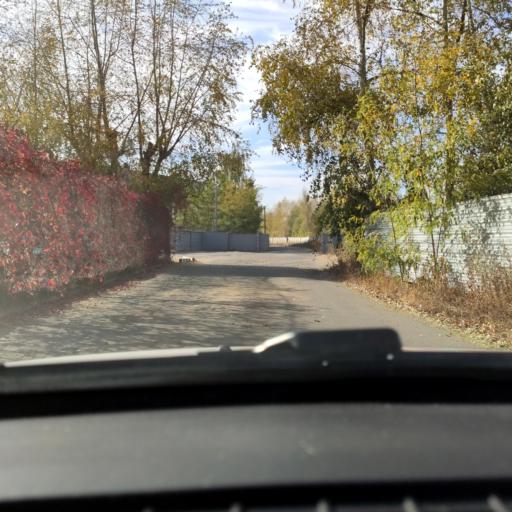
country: RU
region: Voronezj
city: Podgornoye
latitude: 51.8018
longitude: 39.1974
